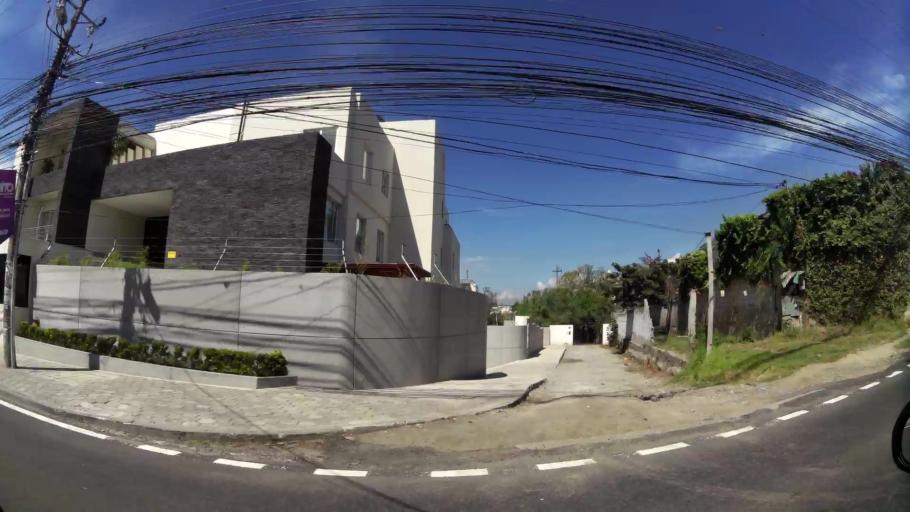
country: EC
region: Pichincha
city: Quito
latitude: -0.2022
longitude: -78.4257
